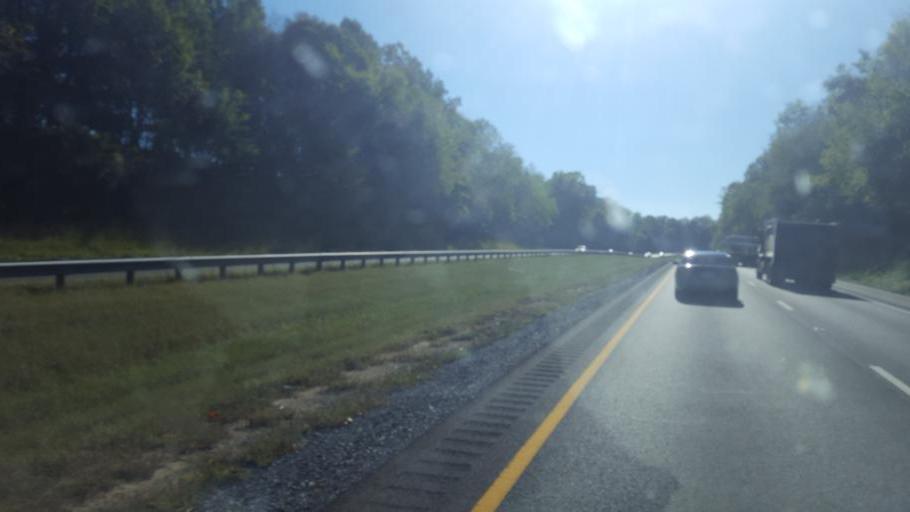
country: US
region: Maryland
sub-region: Frederick County
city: Urbana
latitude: 39.3075
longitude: -77.3447
